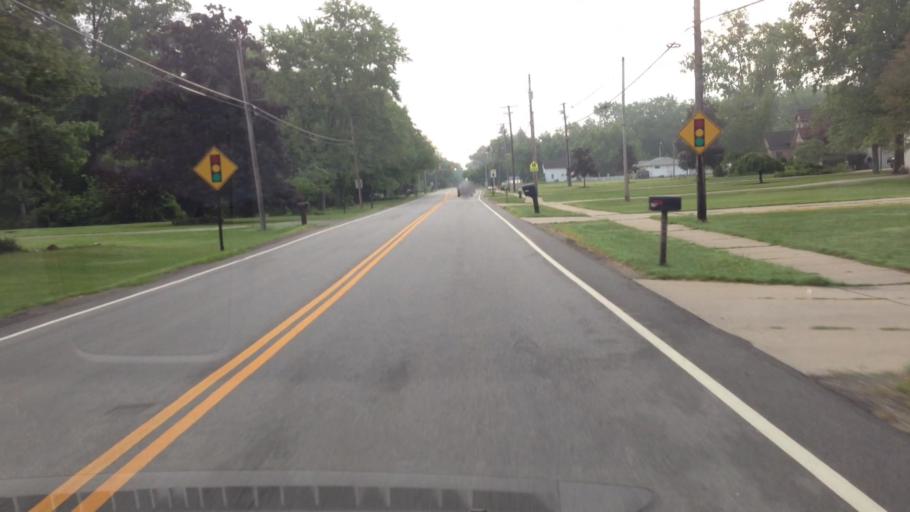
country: US
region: Ohio
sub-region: Cuyahoga County
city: Olmsted Falls
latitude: 41.3727
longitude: -81.9294
